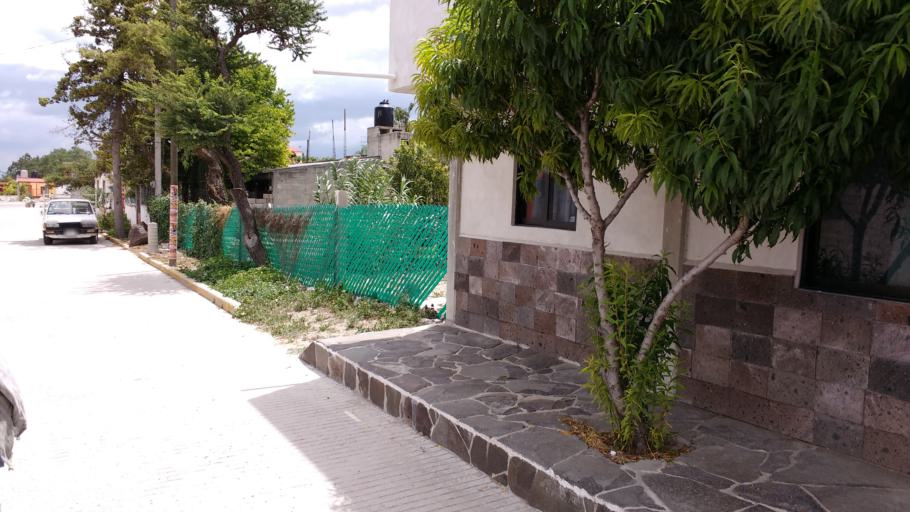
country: MX
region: Hidalgo
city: Mixquiahuala de Juarez
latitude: 20.2273
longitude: -99.2498
